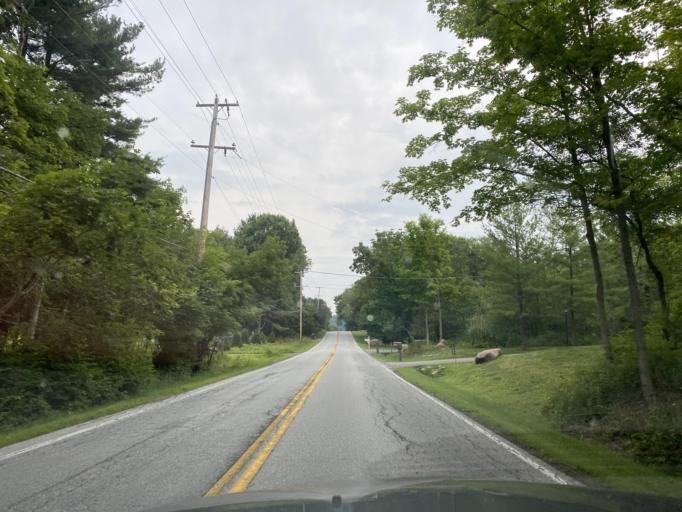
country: US
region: Ohio
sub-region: Summit County
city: Fairlawn
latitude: 41.1517
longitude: -81.5873
